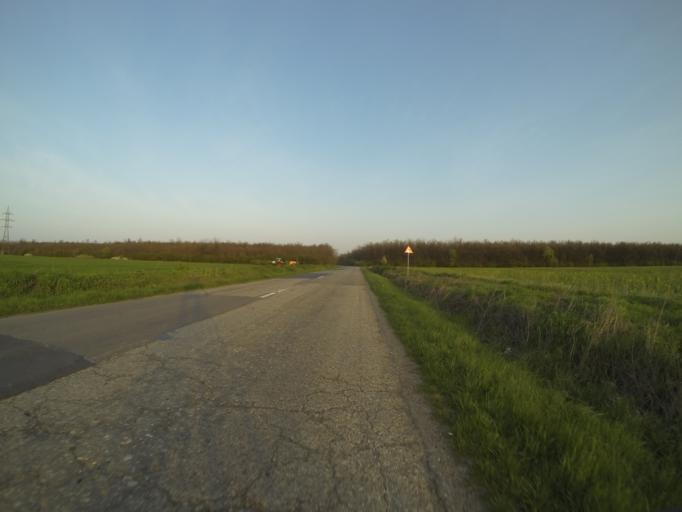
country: RO
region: Dolj
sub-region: Comuna Dranicu
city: Dranic
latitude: 44.0684
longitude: 23.8021
